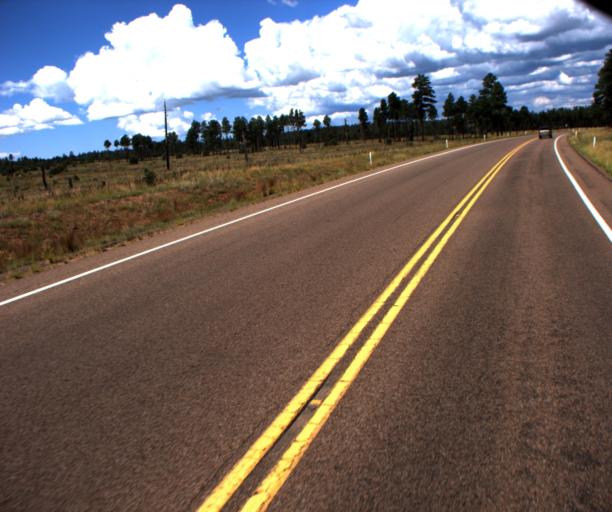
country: US
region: Arizona
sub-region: Navajo County
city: Heber-Overgaard
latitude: 34.3666
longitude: -110.4472
